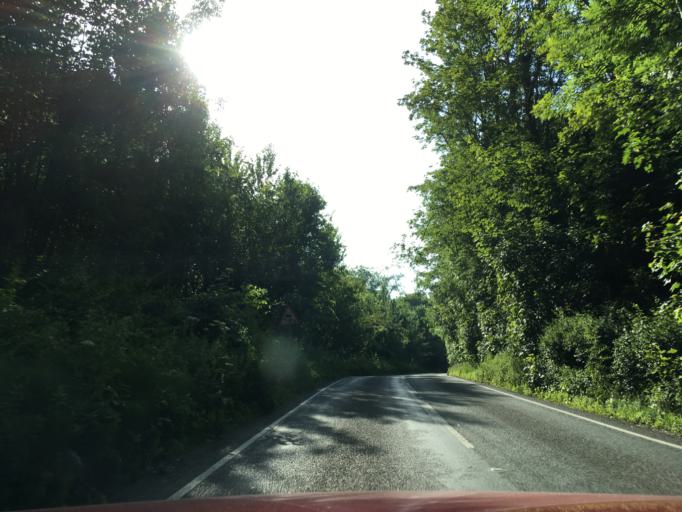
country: GB
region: England
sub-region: Oxfordshire
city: Somerton
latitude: 51.9204
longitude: -1.3119
